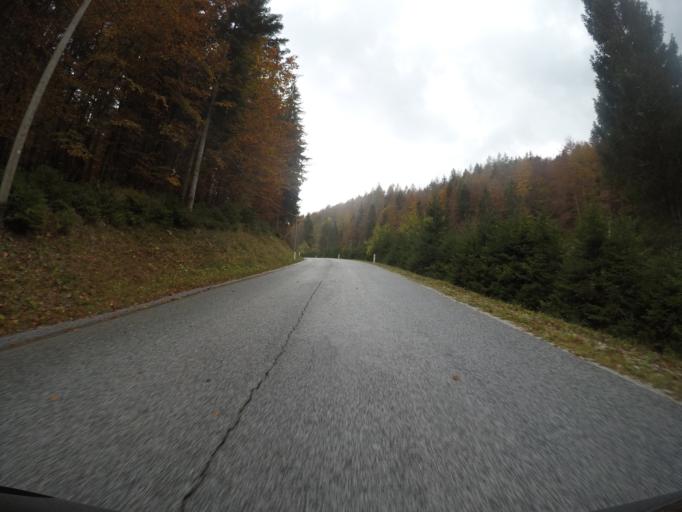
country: SI
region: Kranjska Gora
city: Mojstrana
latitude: 46.4434
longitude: 13.9322
